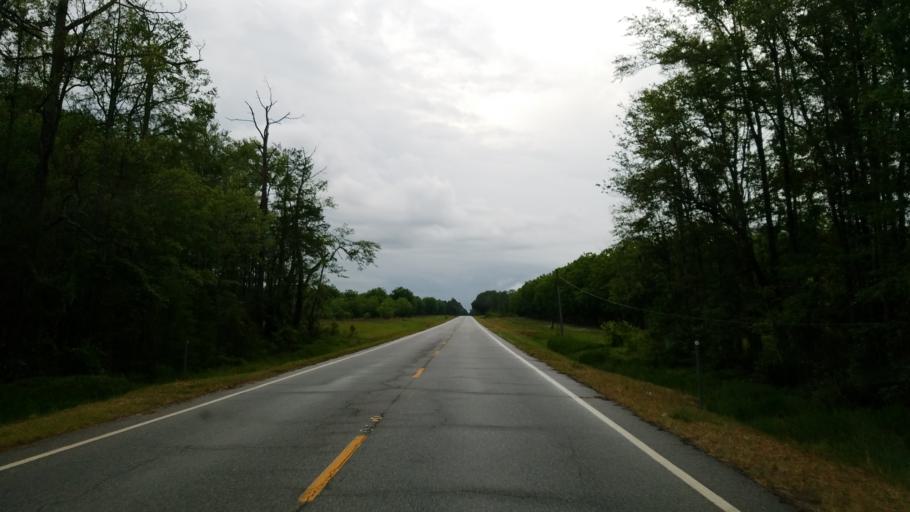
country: US
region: Georgia
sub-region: Berrien County
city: Ray City
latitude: 31.0904
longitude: -83.2489
